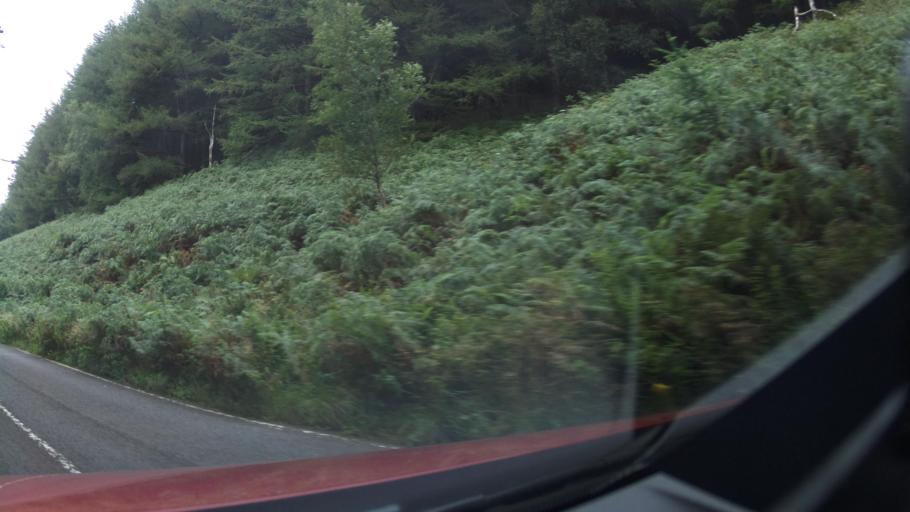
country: GB
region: England
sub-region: Kirklees
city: Meltham
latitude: 53.5024
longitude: -1.8548
